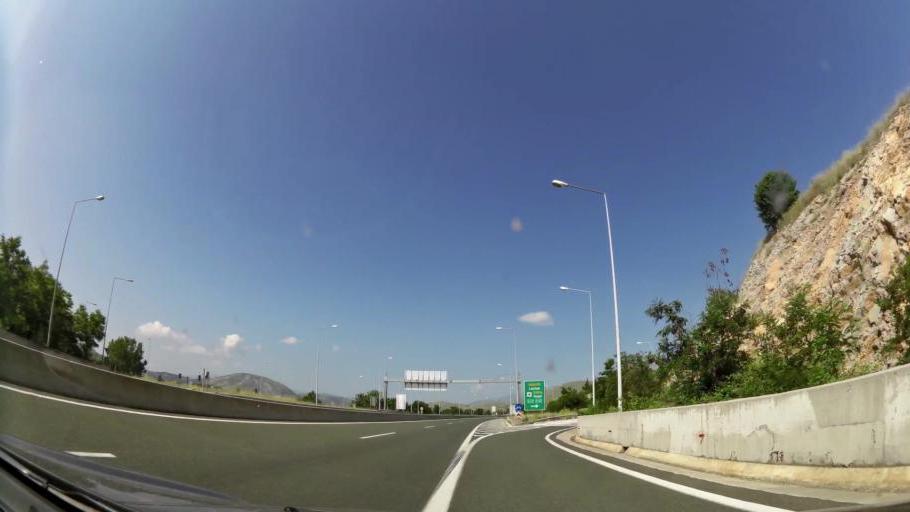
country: GR
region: West Macedonia
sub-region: Nomos Kozanis
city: Koila
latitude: 40.3478
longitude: 21.8032
